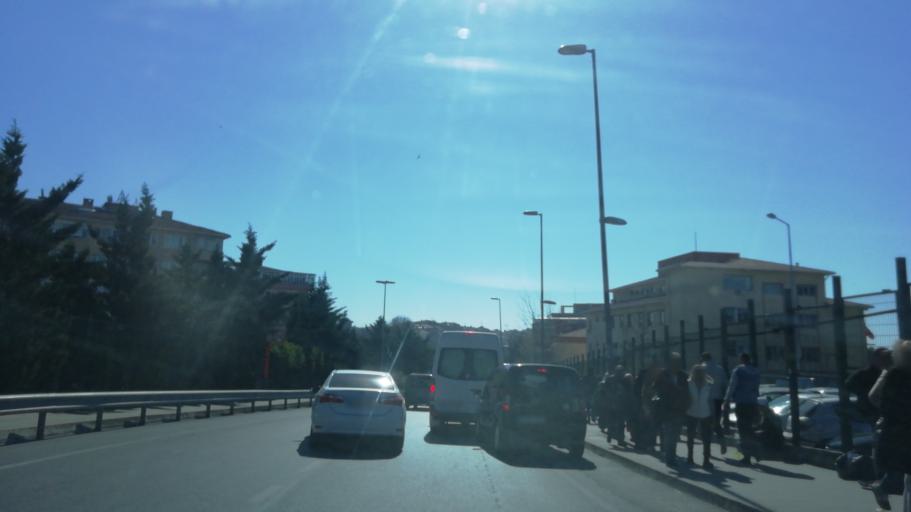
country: TR
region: Istanbul
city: Bahcelievler
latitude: 40.9950
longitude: 28.8649
